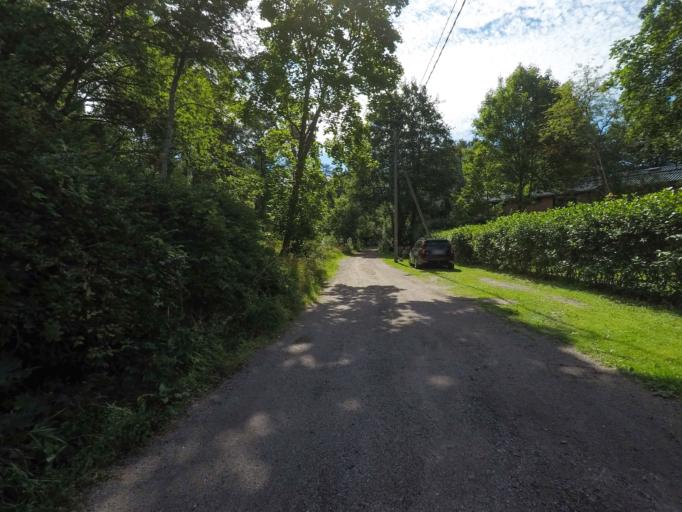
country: FI
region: Uusimaa
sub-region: Helsinki
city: Helsinki
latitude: 60.1615
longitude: 25.0531
